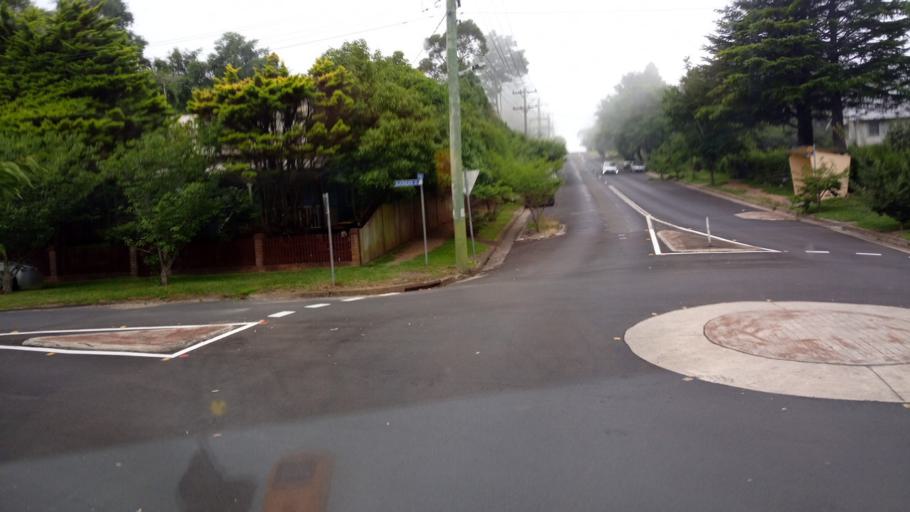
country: AU
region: New South Wales
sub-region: Blue Mountains Municipality
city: Leura
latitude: -33.7148
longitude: 150.3370
